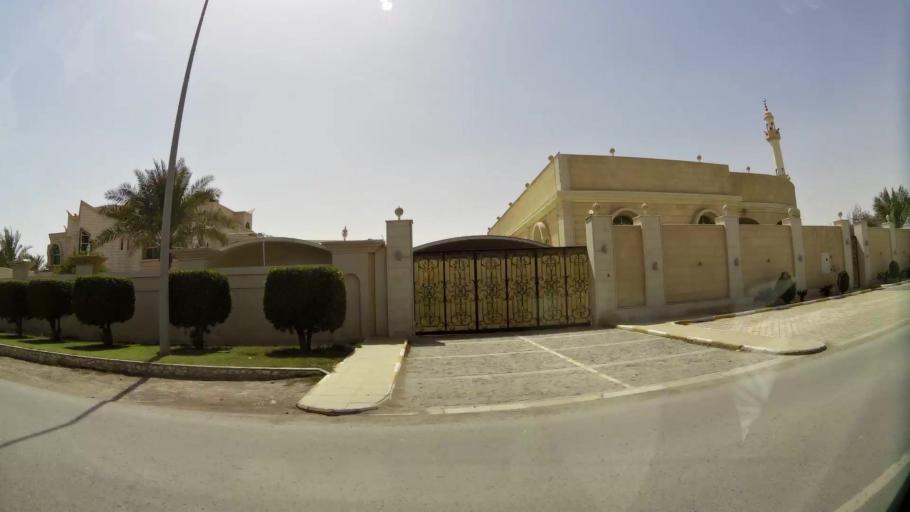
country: QA
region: Baladiyat Umm Salal
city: Umm Salal Muhammad
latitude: 25.3769
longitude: 51.4258
